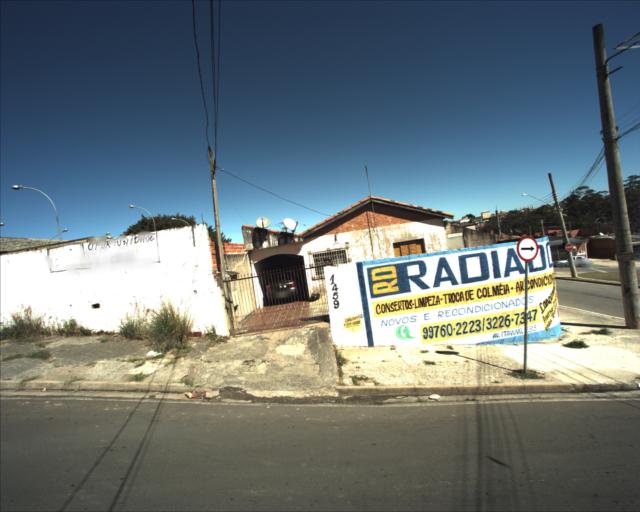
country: BR
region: Sao Paulo
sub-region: Sorocaba
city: Sorocaba
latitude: -23.5031
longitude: -47.4976
